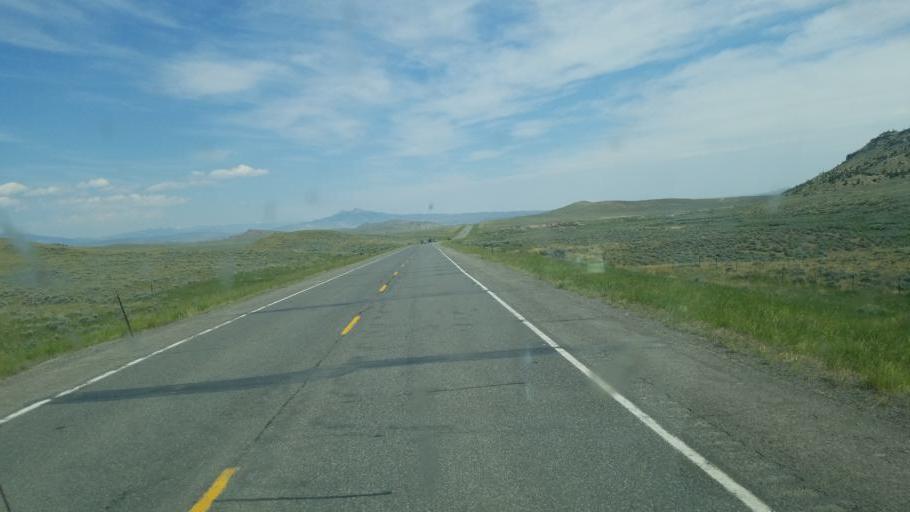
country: US
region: Wyoming
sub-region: Park County
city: Cody
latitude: 44.4162
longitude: -109.0085
